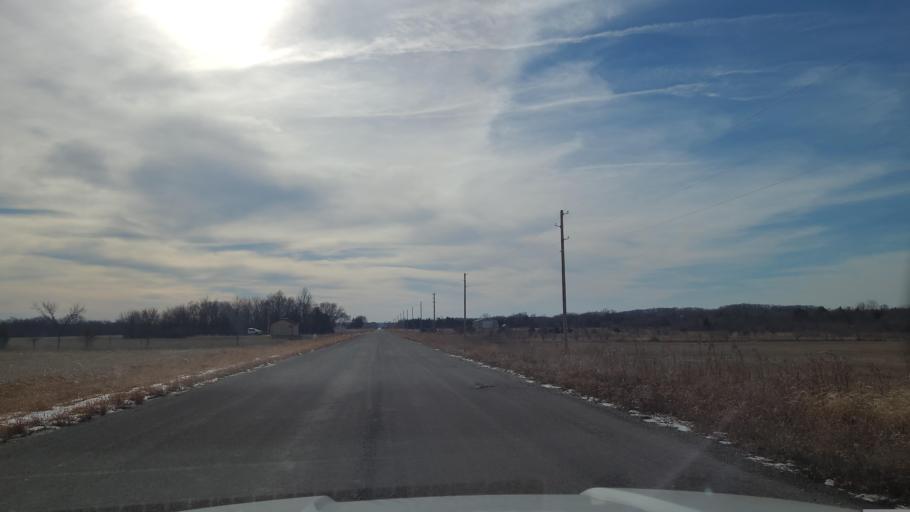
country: US
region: Kansas
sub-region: Douglas County
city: Lawrence
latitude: 38.9077
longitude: -95.2051
